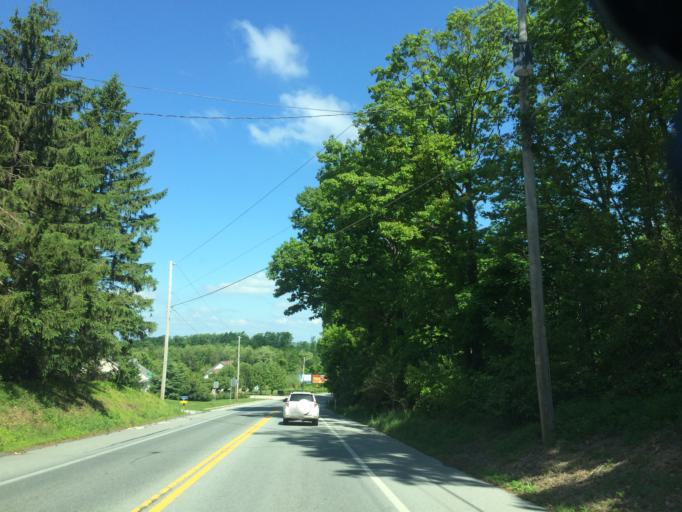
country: US
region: Maryland
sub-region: Carroll County
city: Manchester
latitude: 39.7241
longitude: -76.9196
